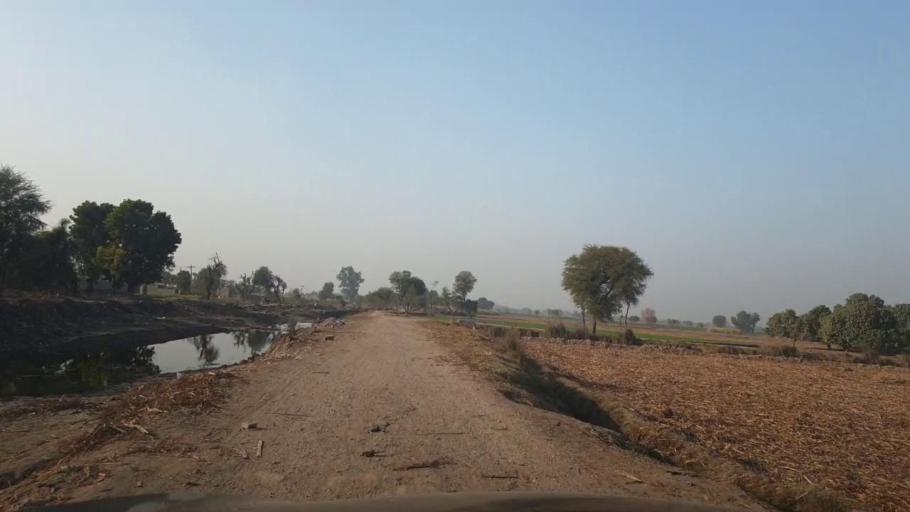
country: PK
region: Sindh
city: Ubauro
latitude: 28.2979
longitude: 69.8019
